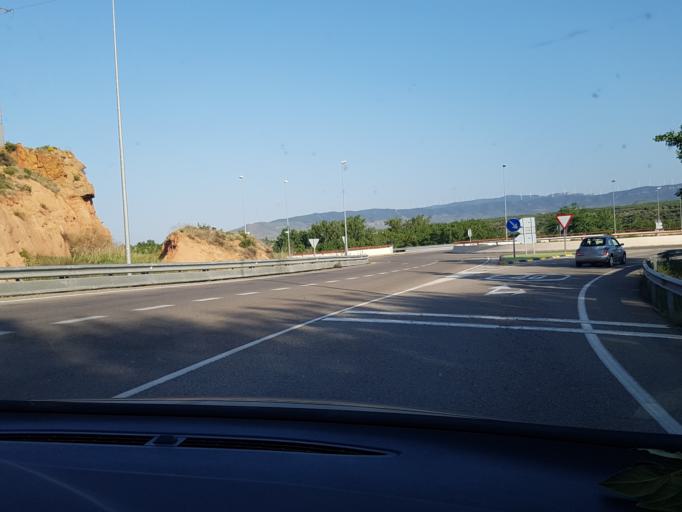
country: ES
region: La Rioja
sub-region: Provincia de La Rioja
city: Arnedo
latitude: 42.2329
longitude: -2.0776
